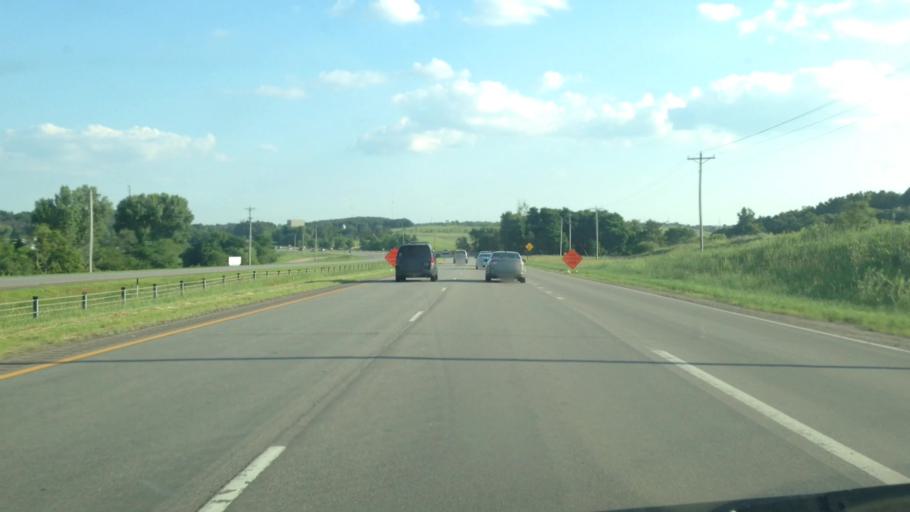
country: US
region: Minnesota
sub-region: Sherburne County
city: Elk River
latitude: 45.3706
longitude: -93.5639
